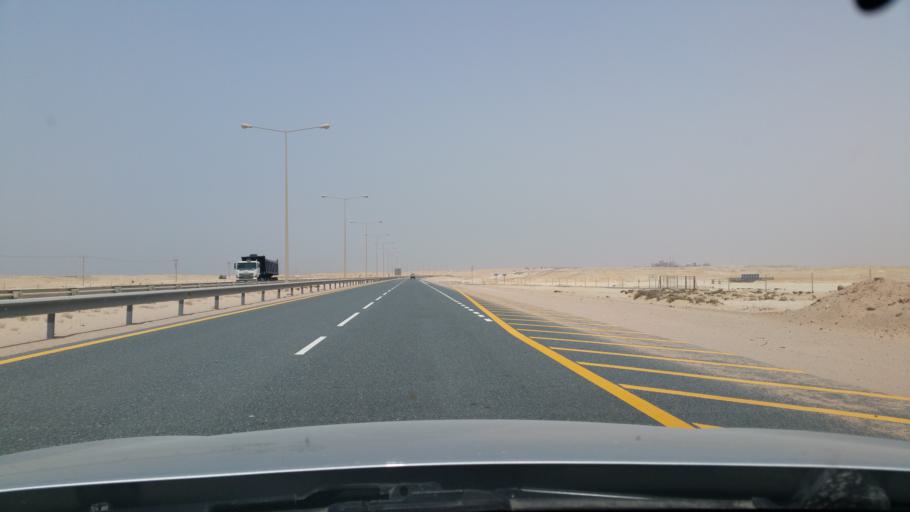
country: QA
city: Umm Bab
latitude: 25.1637
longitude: 50.8165
